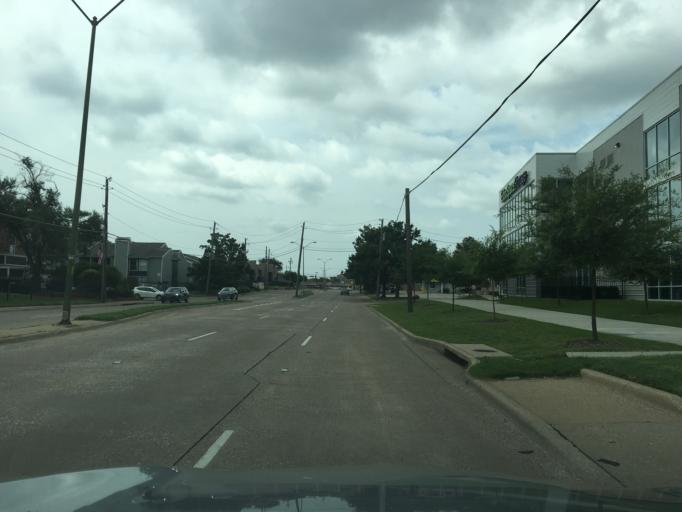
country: US
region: Texas
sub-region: Dallas County
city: Addison
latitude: 32.9361
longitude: -96.8138
